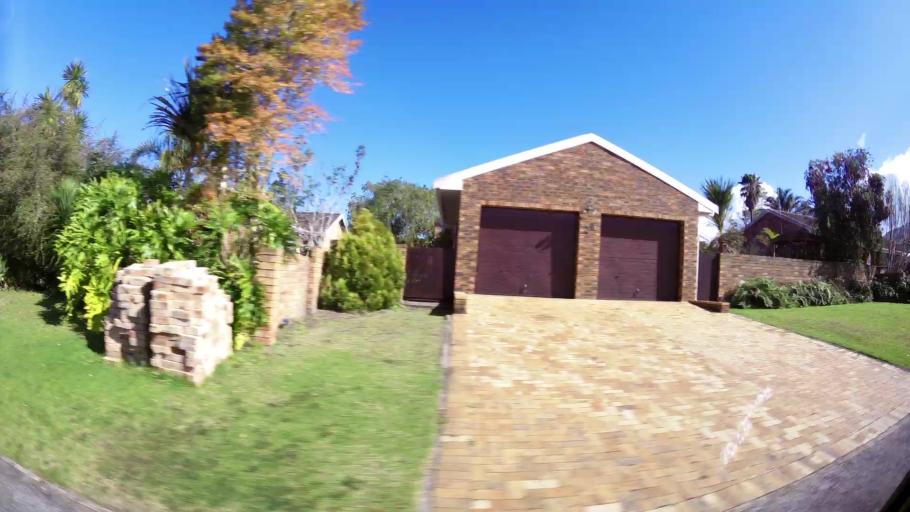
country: ZA
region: Western Cape
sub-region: Eden District Municipality
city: George
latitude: -33.9487
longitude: 22.4796
